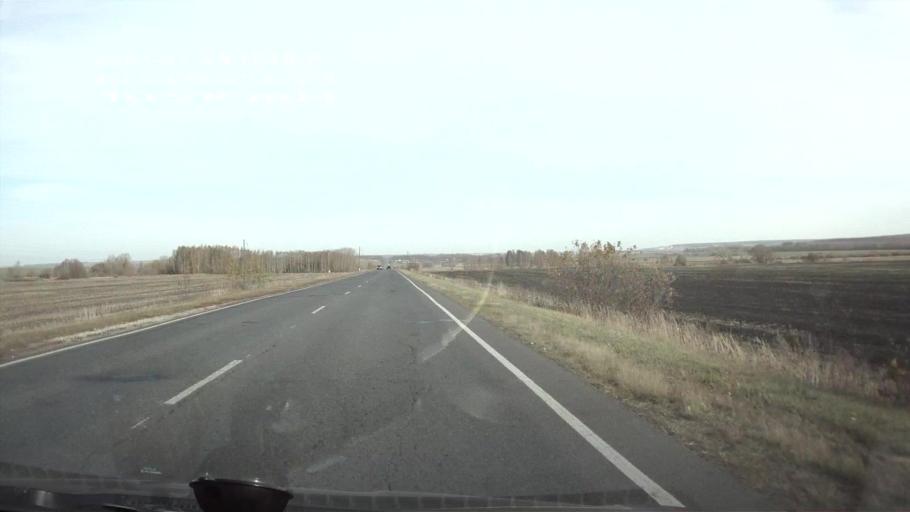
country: RU
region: Mordoviya
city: Atyashevo
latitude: 54.5417
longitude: 45.9372
